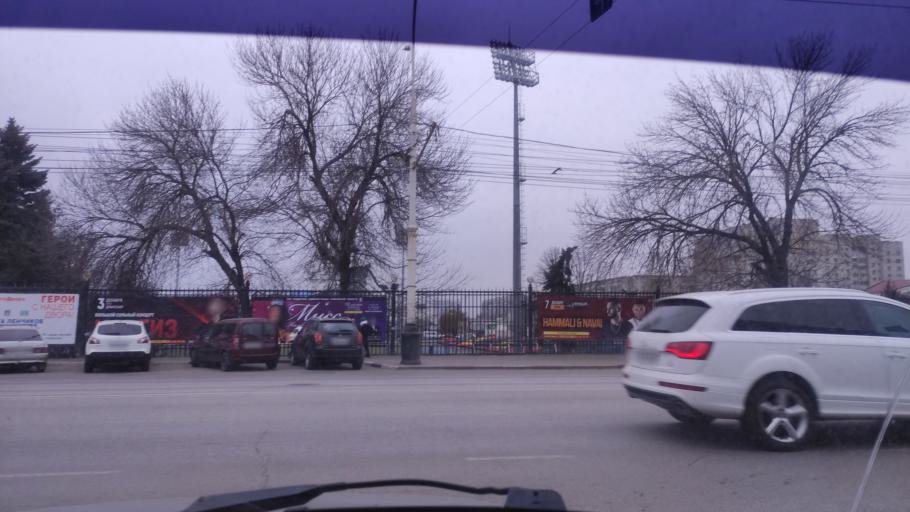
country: RU
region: Tambov
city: Tambov
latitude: 52.7285
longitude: 41.4548
